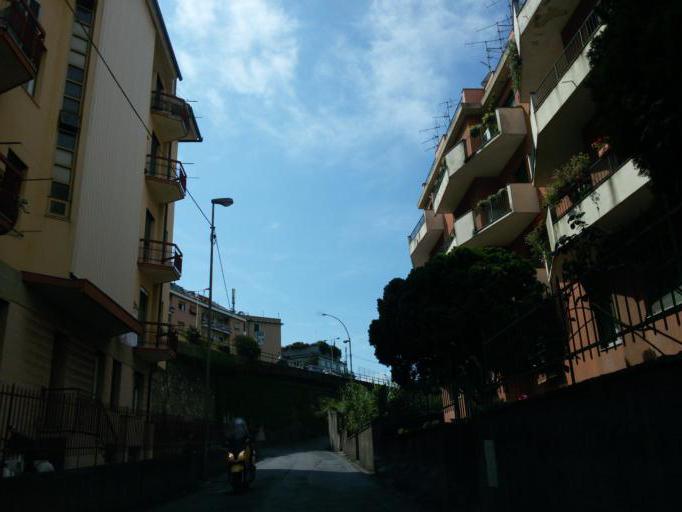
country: IT
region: Liguria
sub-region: Provincia di Genova
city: Bogliasco
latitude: 44.3982
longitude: 8.9931
